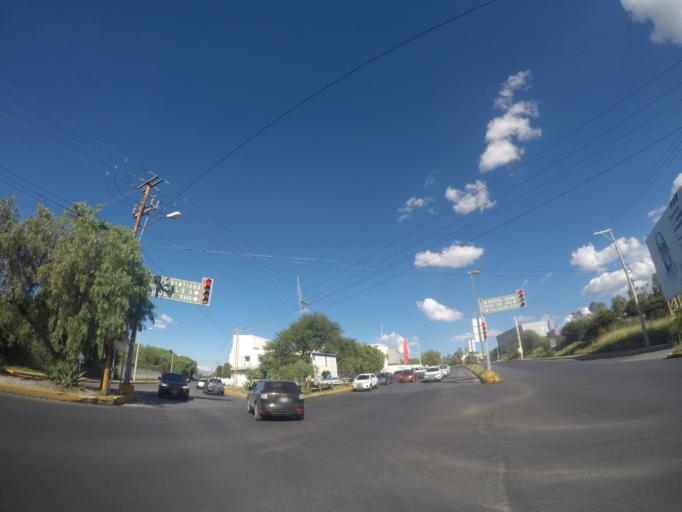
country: MX
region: San Luis Potosi
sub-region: Mexquitic de Carmona
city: Guadalupe Victoria
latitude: 22.1511
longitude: -101.0283
